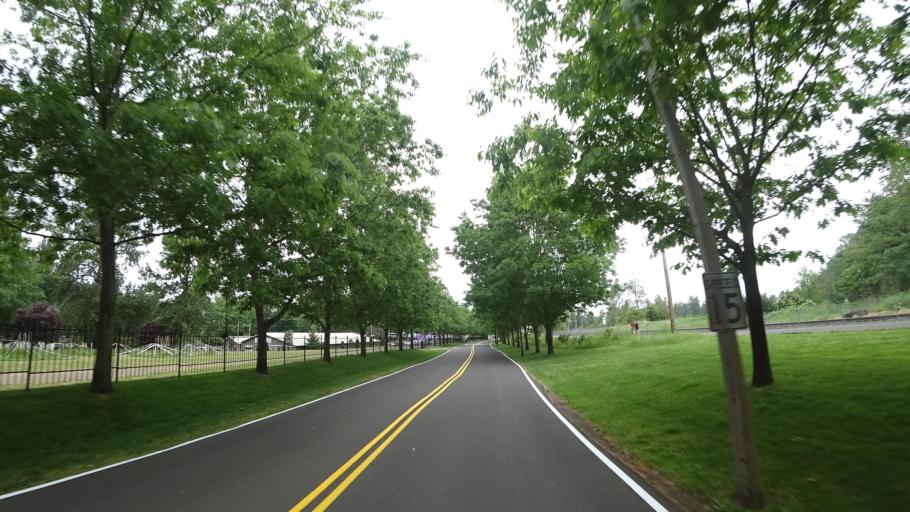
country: US
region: Oregon
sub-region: Clackamas County
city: Milwaukie
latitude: 45.4688
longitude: -122.6626
